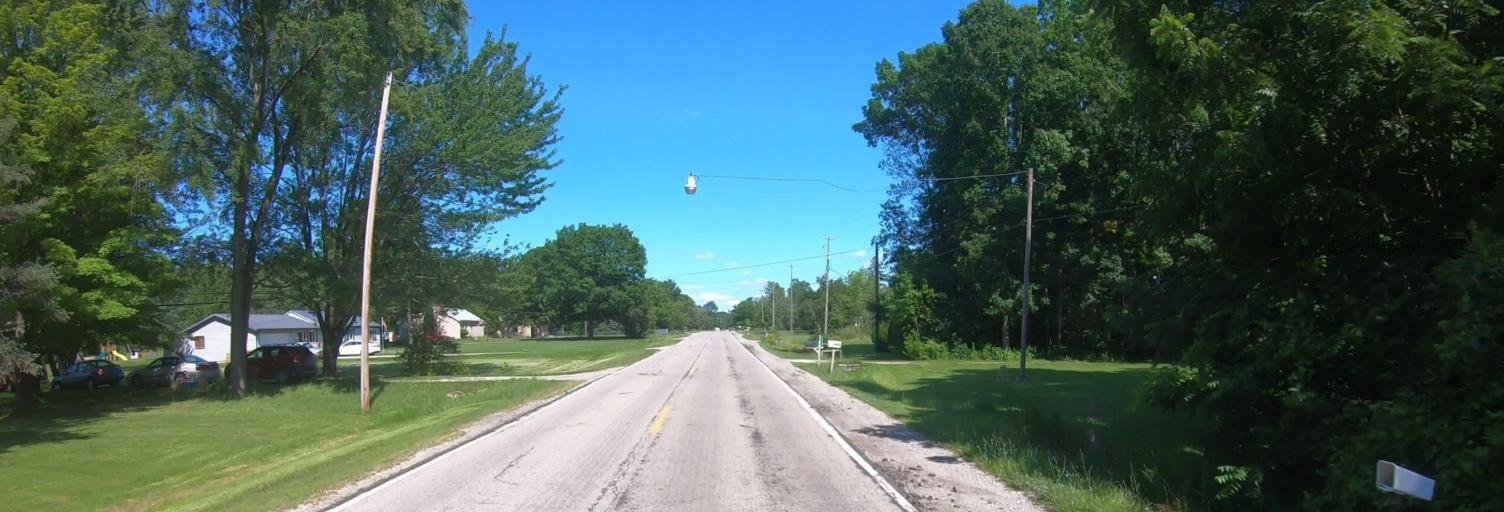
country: US
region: Michigan
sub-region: Genesee County
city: Flushing
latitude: 43.0786
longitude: -83.7817
